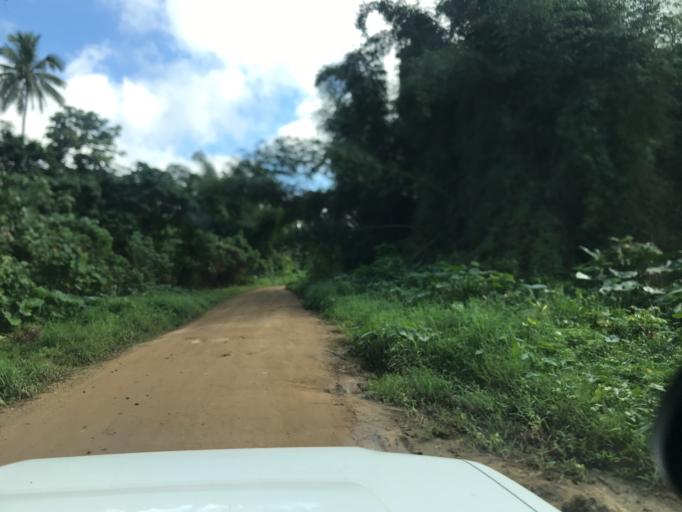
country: VU
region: Sanma
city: Luganville
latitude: -15.4962
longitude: 167.0899
